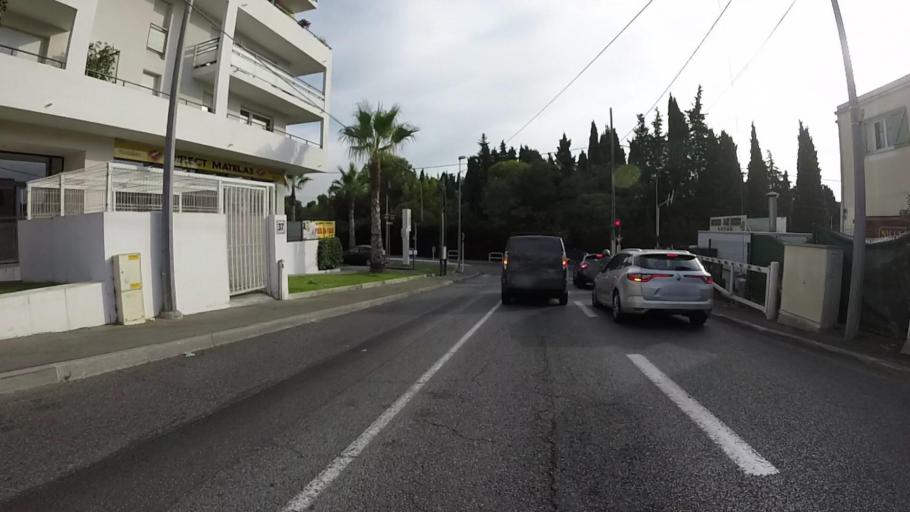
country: FR
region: Provence-Alpes-Cote d'Azur
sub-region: Departement des Alpes-Maritimes
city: Antibes
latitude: 43.5904
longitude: 7.1061
